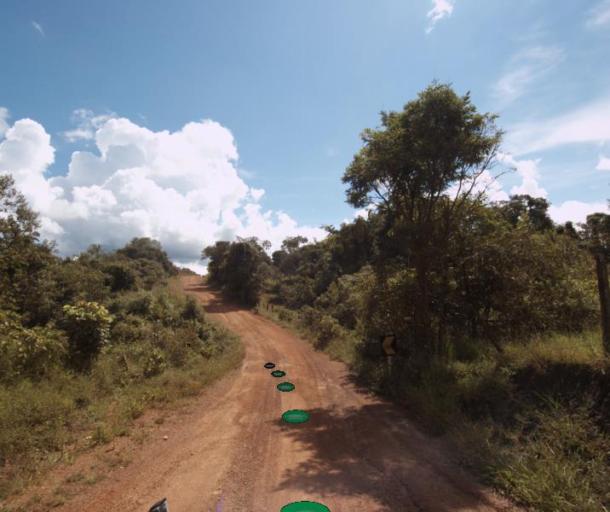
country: BR
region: Goias
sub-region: Pirenopolis
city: Pirenopolis
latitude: -15.7811
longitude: -48.8163
